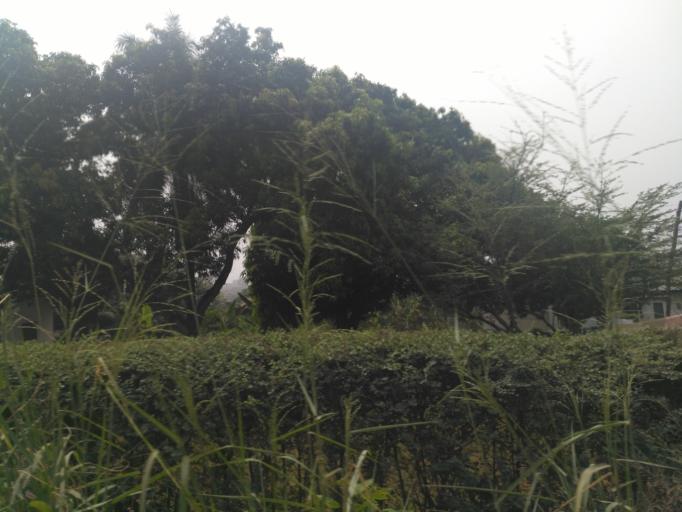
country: GH
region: Ashanti
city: Kumasi
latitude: 6.6831
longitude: -1.6352
